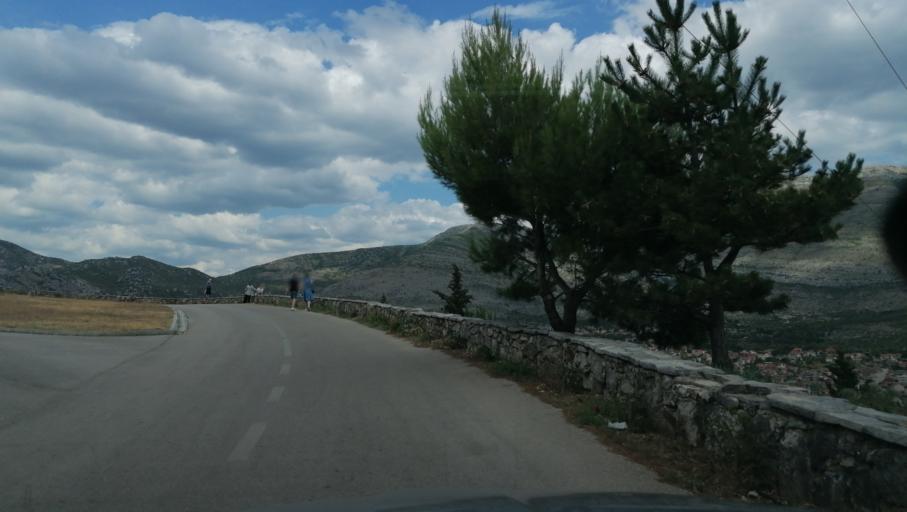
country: BA
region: Republika Srpska
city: Trebinje
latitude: 42.7115
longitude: 18.3612
